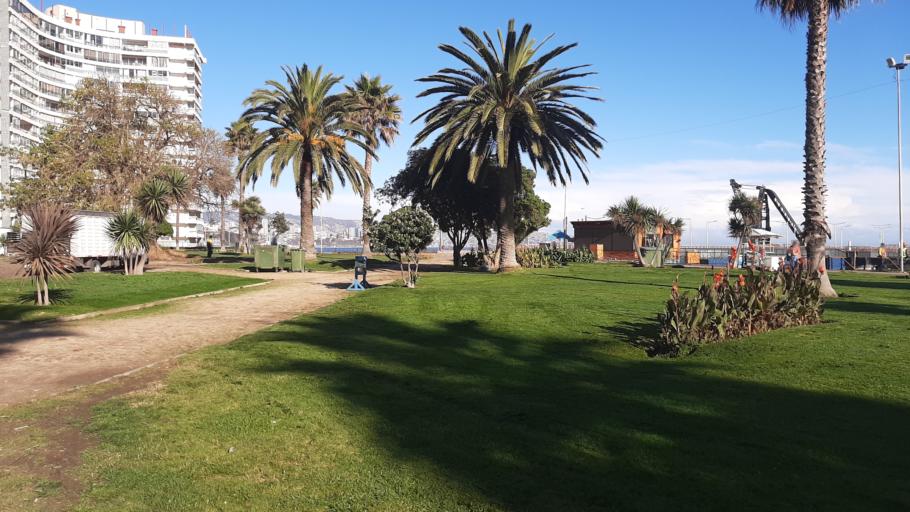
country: CL
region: Valparaiso
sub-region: Provincia de Valparaiso
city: Vina del Mar
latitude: -33.0114
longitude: -71.5529
